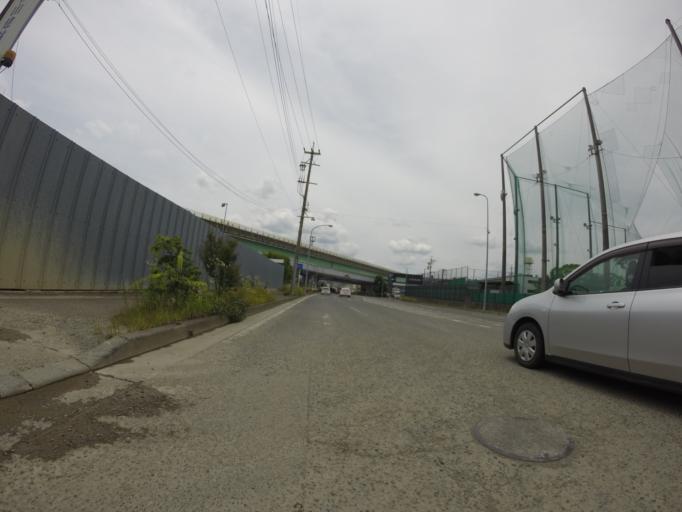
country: JP
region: Shizuoka
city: Shizuoka-shi
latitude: 35.0082
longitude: 138.4129
